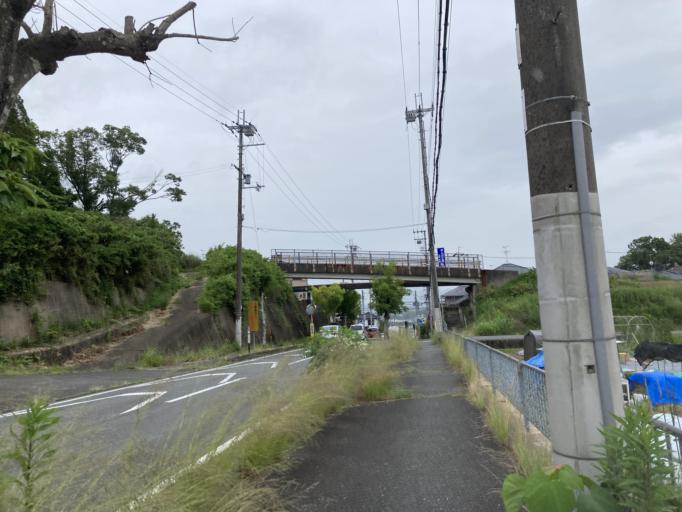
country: JP
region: Nara
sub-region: Ikoma-shi
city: Ikoma
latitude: 34.6354
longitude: 135.7066
